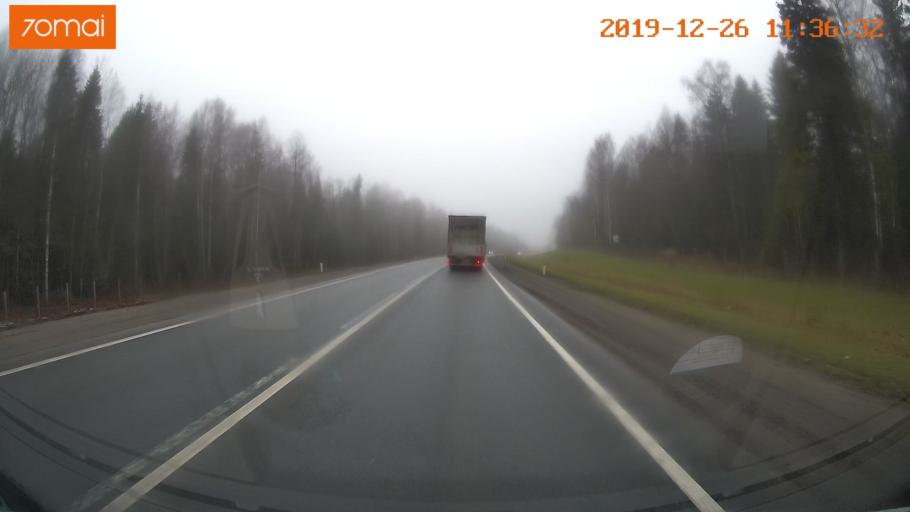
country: RU
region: Vologda
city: Sheksna
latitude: 59.1939
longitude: 38.6455
